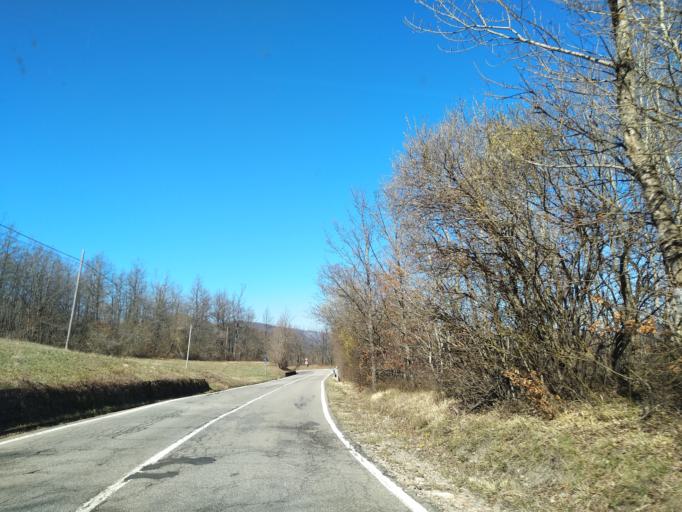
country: IT
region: Emilia-Romagna
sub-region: Provincia di Reggio Emilia
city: Ramiseto
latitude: 44.4075
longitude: 10.3129
